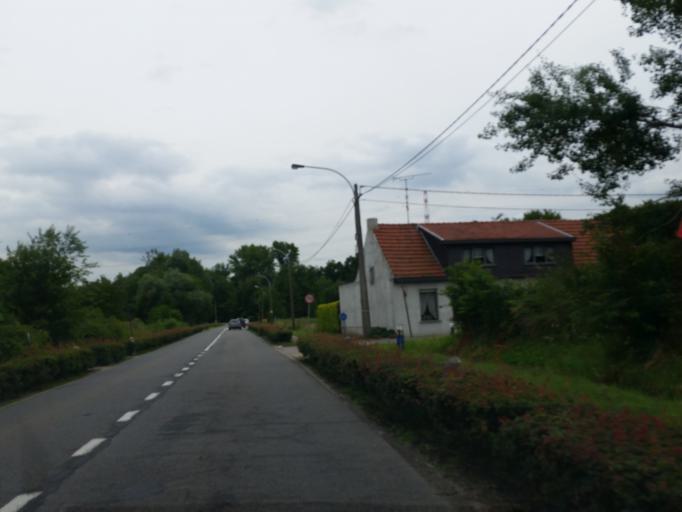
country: BE
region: Flanders
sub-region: Provincie Antwerpen
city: Ranst
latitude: 51.2016
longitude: 4.5981
